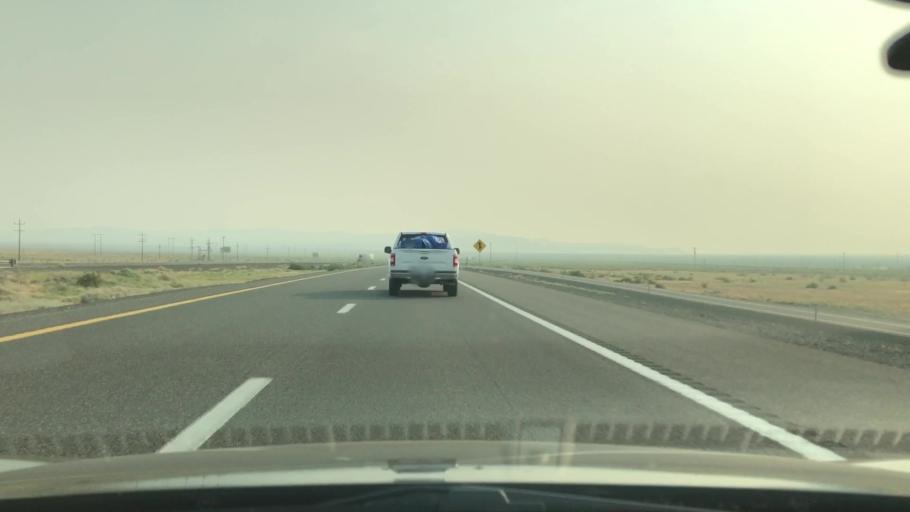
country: US
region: Nevada
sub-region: Pershing County
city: Lovelock
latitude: 40.0612
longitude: -118.6512
